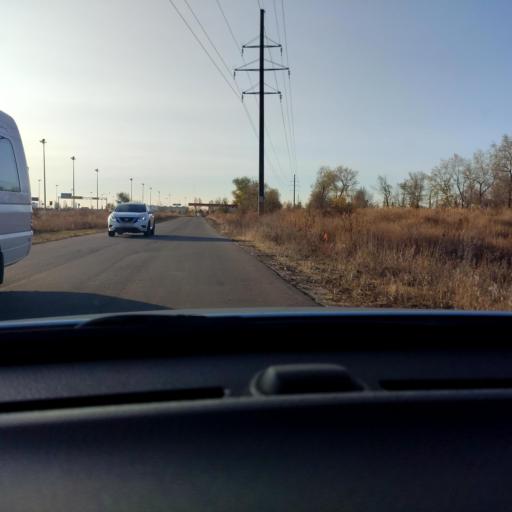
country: RU
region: Voronezj
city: Somovo
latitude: 51.6591
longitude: 39.3013
